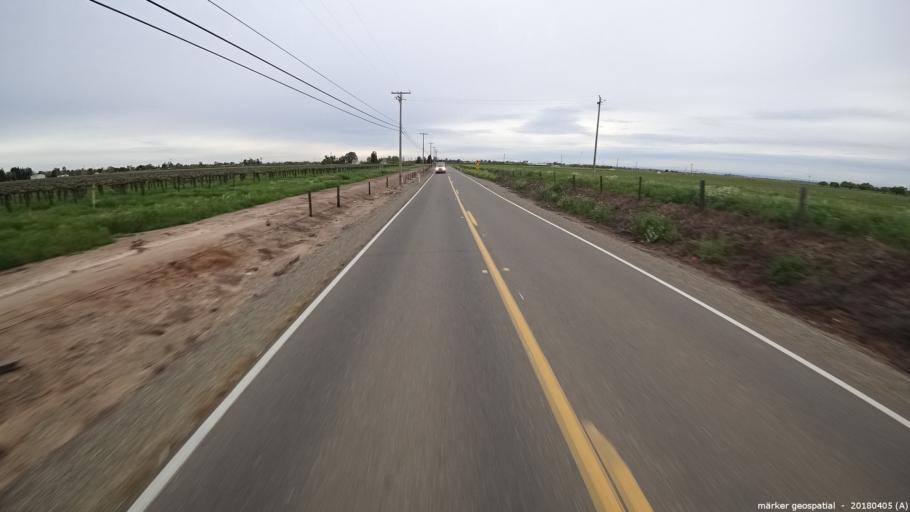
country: US
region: California
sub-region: Sacramento County
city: Herald
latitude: 38.3185
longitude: -121.2263
